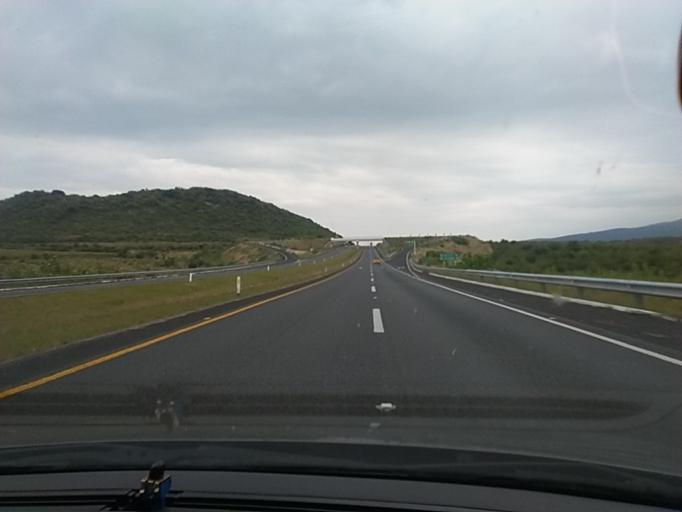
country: MX
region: Michoacan
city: Penjamillo de Degollado
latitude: 20.0429
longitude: -101.9381
